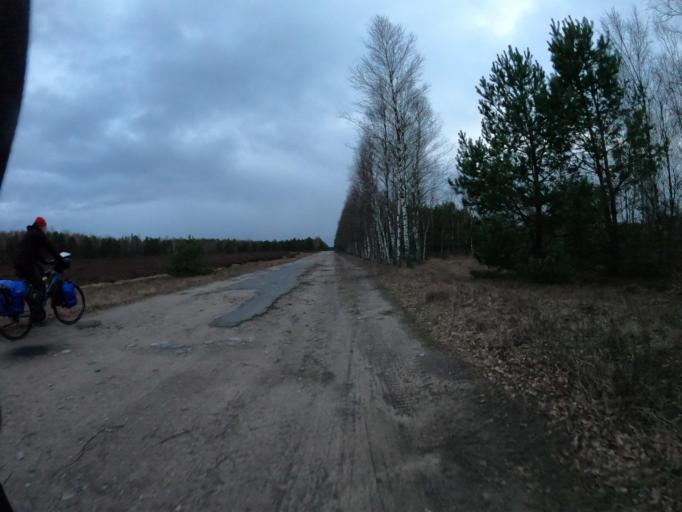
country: PL
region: West Pomeranian Voivodeship
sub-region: Powiat szczecinecki
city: Borne Sulinowo
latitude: 53.5263
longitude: 16.5699
